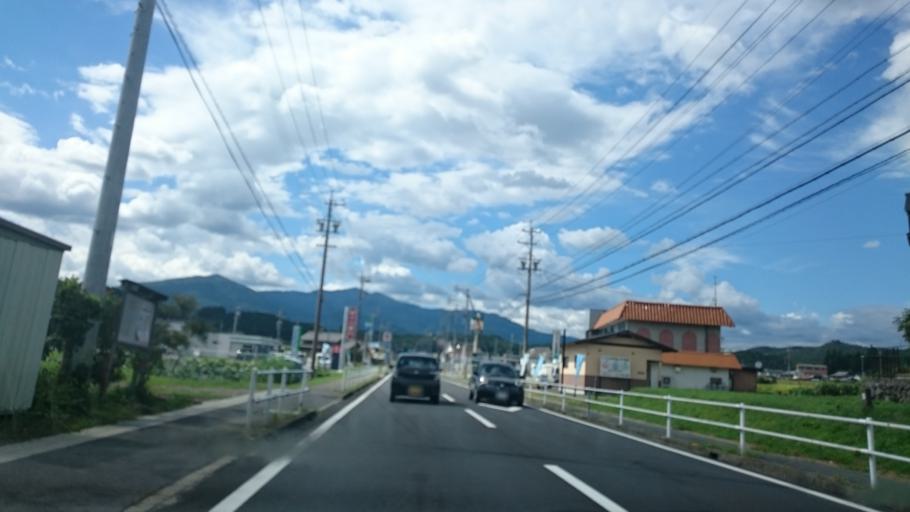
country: JP
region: Gifu
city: Nakatsugawa
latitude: 35.5240
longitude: 137.4707
